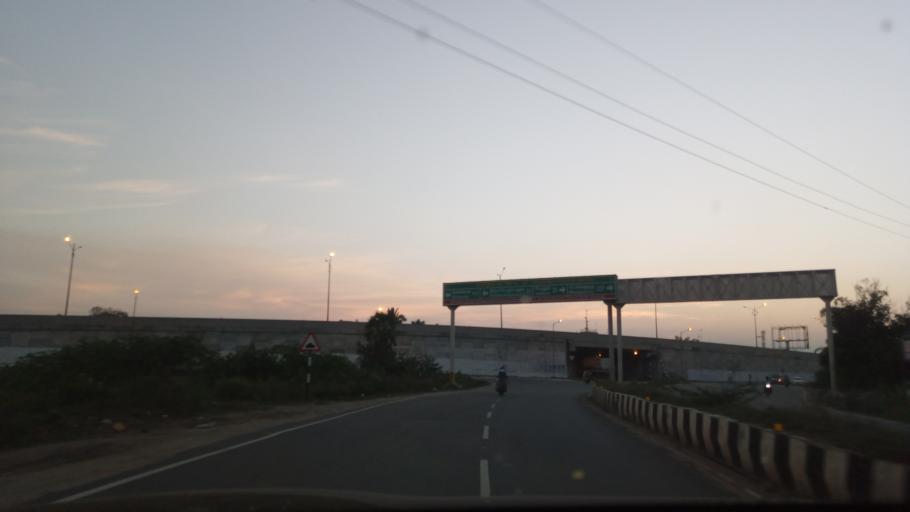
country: IN
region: Tamil Nadu
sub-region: Vellore
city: Walajapet
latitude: 12.9197
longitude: 79.3423
